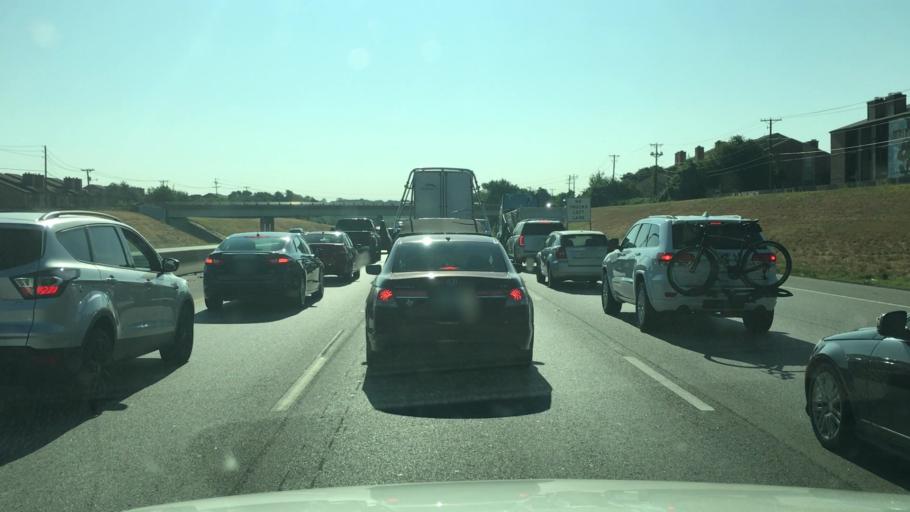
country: US
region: Texas
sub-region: Tarrant County
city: Pantego
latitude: 32.7601
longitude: -97.1606
